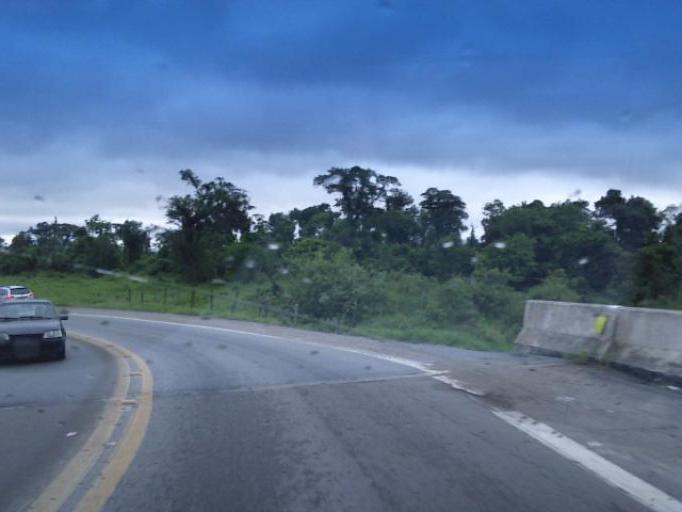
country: BR
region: Santa Catarina
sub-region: Itajai
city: Itajai
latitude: -26.9192
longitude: -48.7108
